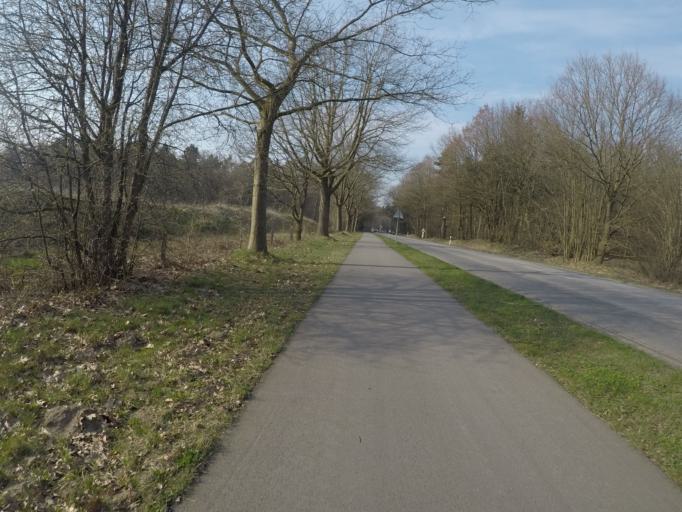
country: DE
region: Schleswig-Holstein
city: Wittenborn
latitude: 53.9442
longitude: 10.2212
